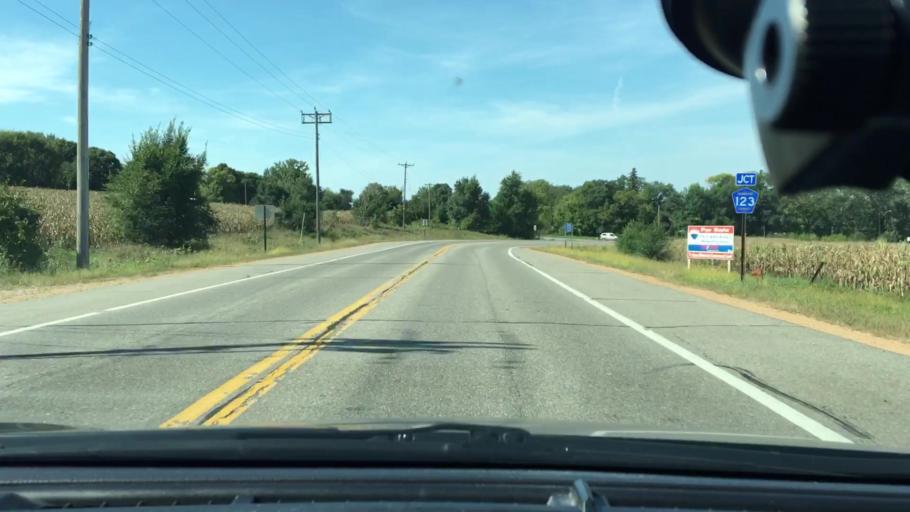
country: US
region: Minnesota
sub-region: Wright County
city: Hanover
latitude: 45.1524
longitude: -93.6634
